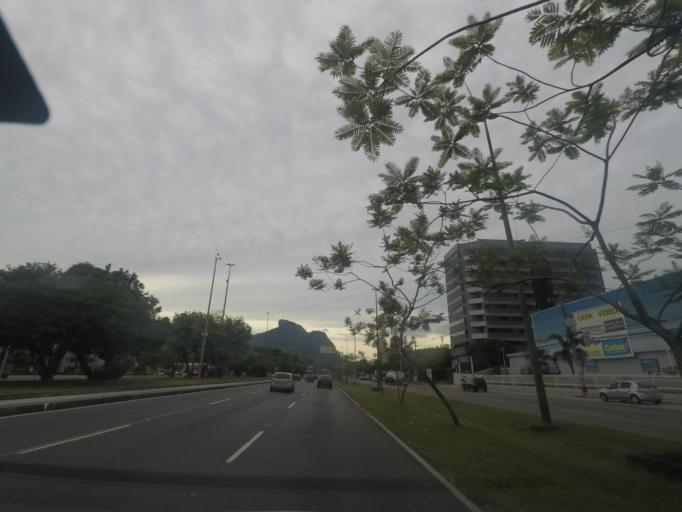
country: BR
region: Rio de Janeiro
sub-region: Rio De Janeiro
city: Rio de Janeiro
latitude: -23.0006
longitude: -43.3382
